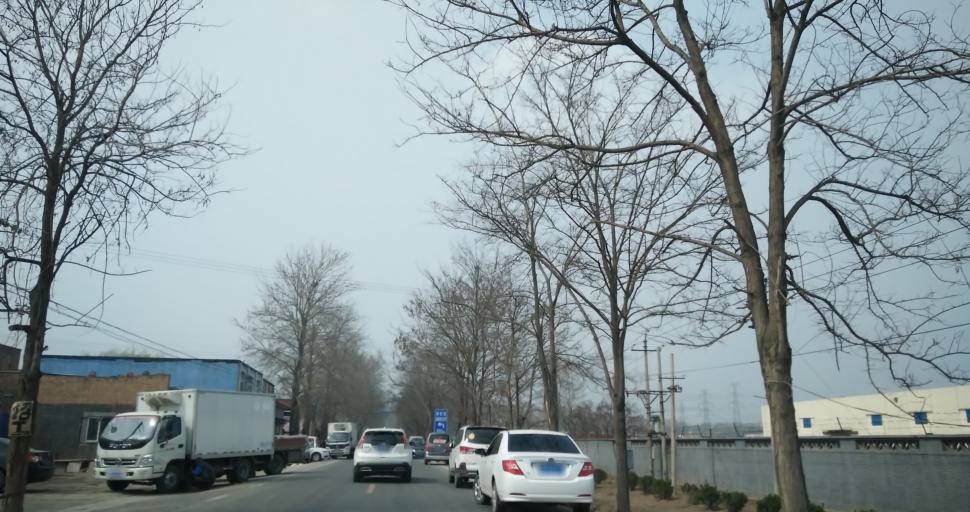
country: CN
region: Beijing
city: Qingyundian
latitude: 39.6895
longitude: 116.4944
